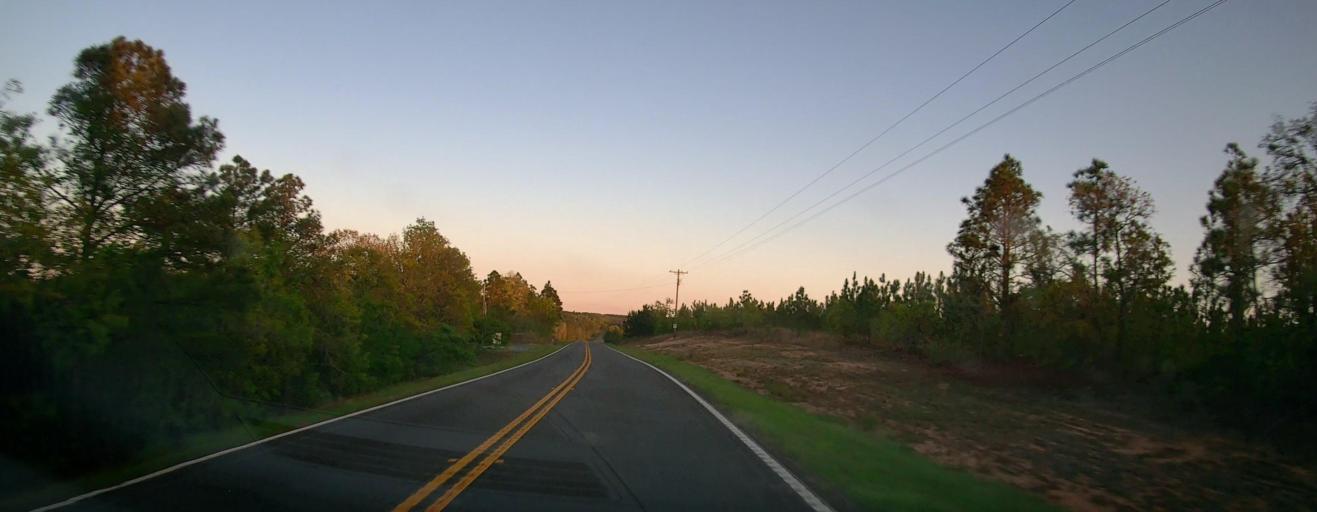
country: US
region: Georgia
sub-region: Marion County
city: Buena Vista
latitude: 32.4044
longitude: -84.5808
